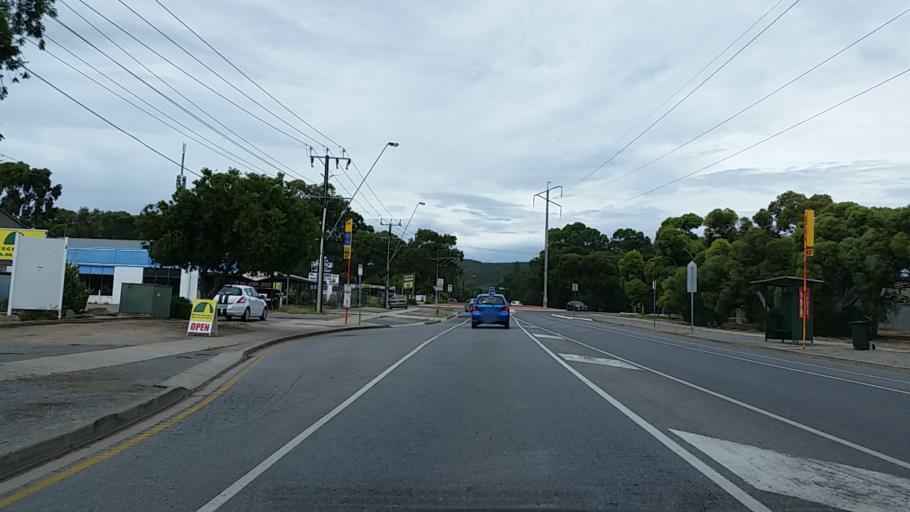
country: AU
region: South Australia
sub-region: Tea Tree Gully
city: Hope Valley
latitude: -34.8324
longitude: 138.7058
